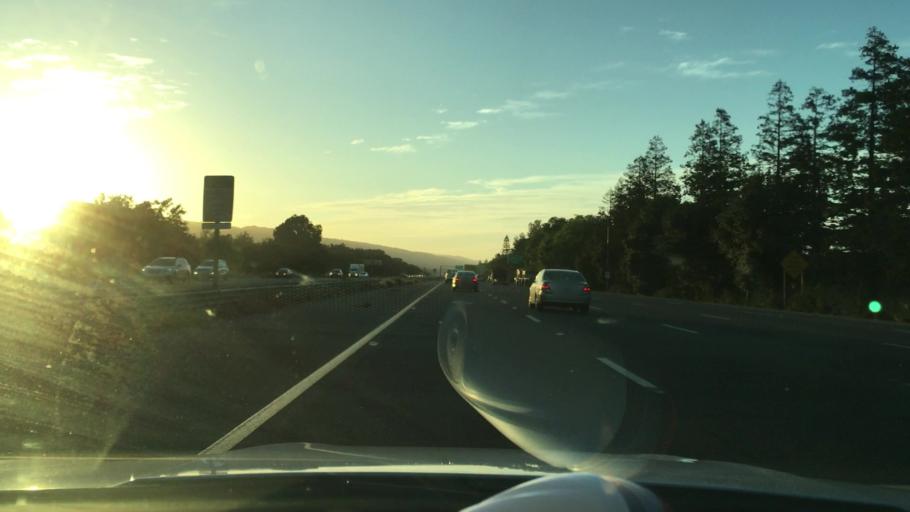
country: US
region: California
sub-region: Santa Clara County
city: Seven Trees
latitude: 37.2554
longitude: -121.7935
